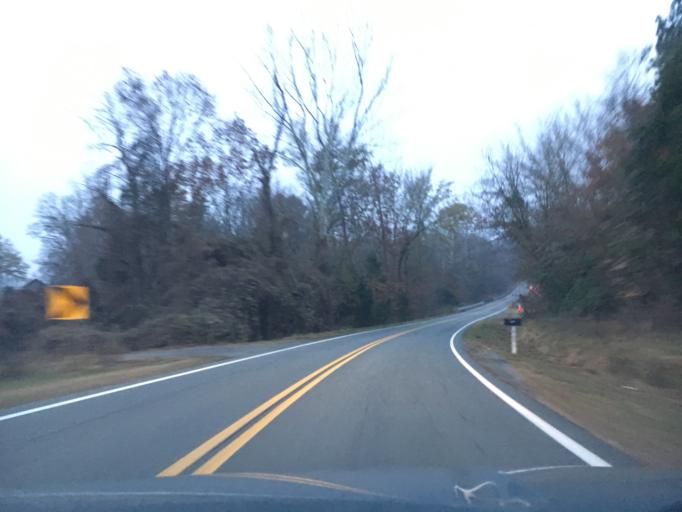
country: US
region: Virginia
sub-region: Halifax County
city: Mountain Road
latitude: 36.6976
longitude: -78.9728
